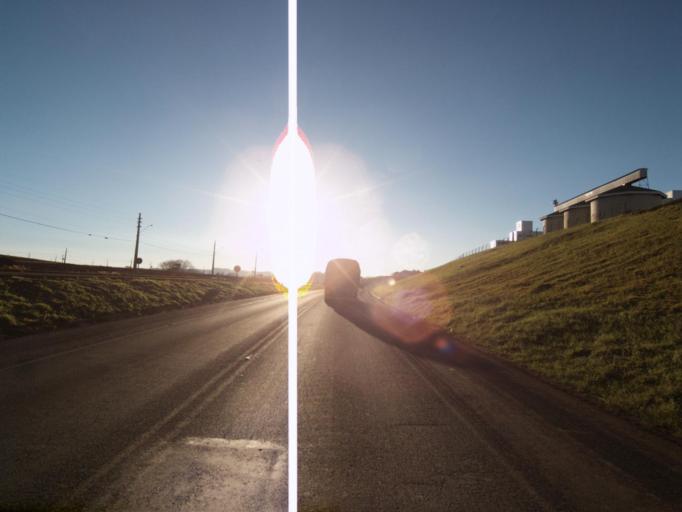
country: BR
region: Santa Catarina
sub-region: Chapeco
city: Chapeco
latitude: -26.8353
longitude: -52.9907
